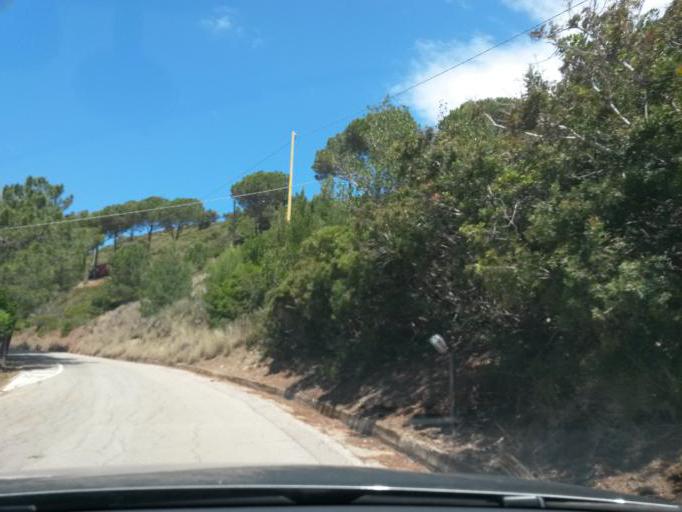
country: IT
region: Tuscany
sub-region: Provincia di Livorno
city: Marciana
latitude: 42.7937
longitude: 10.1125
